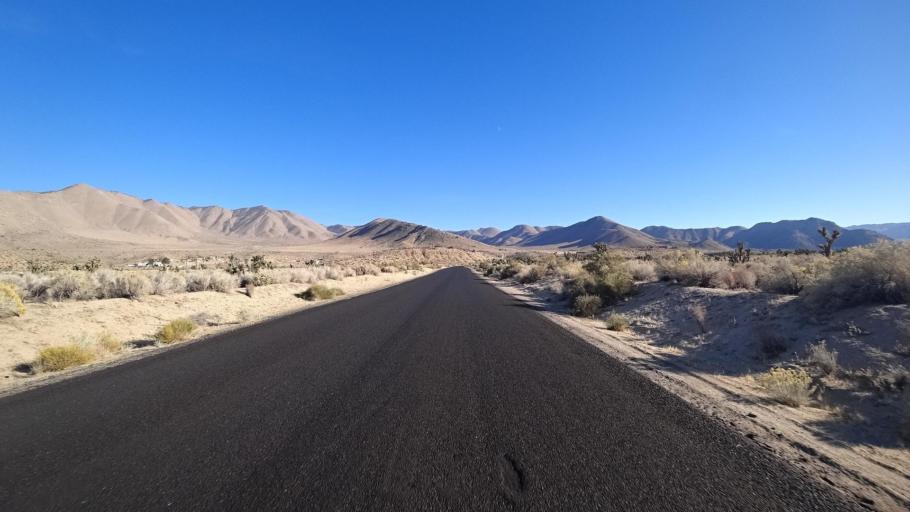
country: US
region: California
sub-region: Kern County
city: Weldon
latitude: 35.6134
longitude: -118.2464
